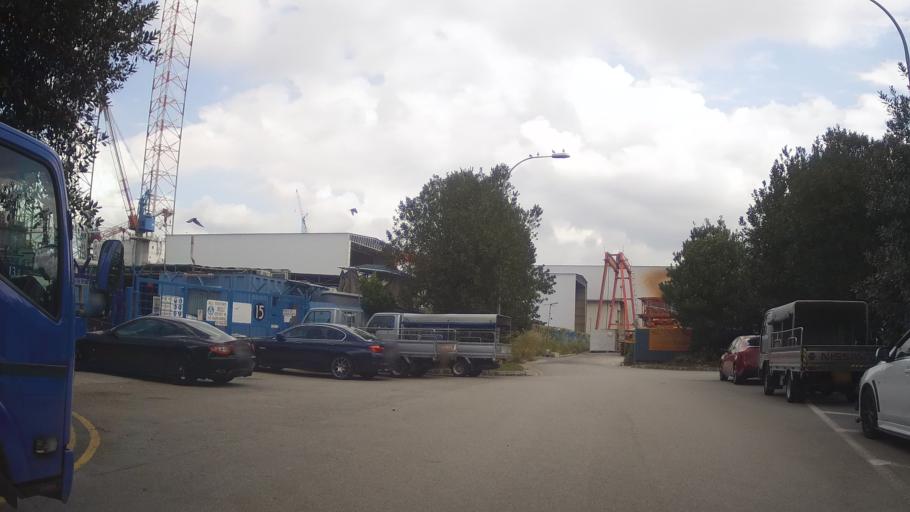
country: MY
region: Johor
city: Johor Bahru
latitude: 1.3098
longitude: 103.6485
